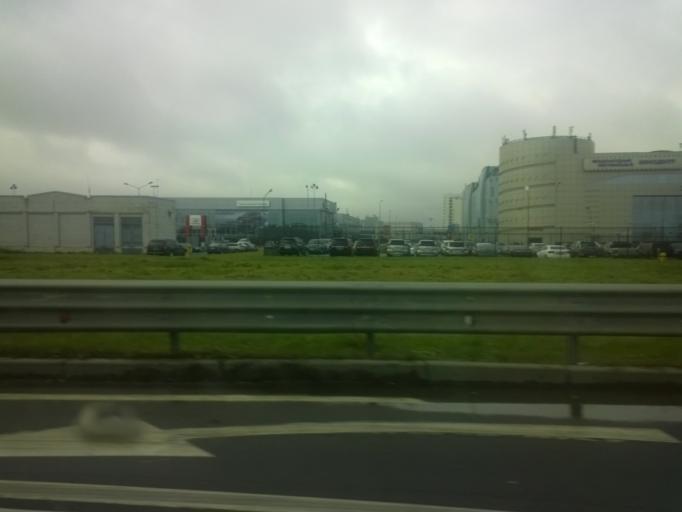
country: RU
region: St.-Petersburg
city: Kupchino
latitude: 59.8054
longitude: 30.3235
